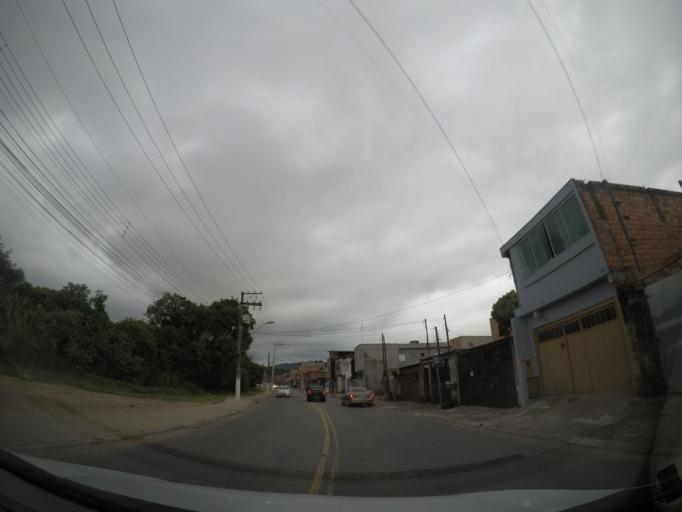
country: BR
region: Sao Paulo
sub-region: Aruja
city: Aruja
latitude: -23.3997
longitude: -46.4258
